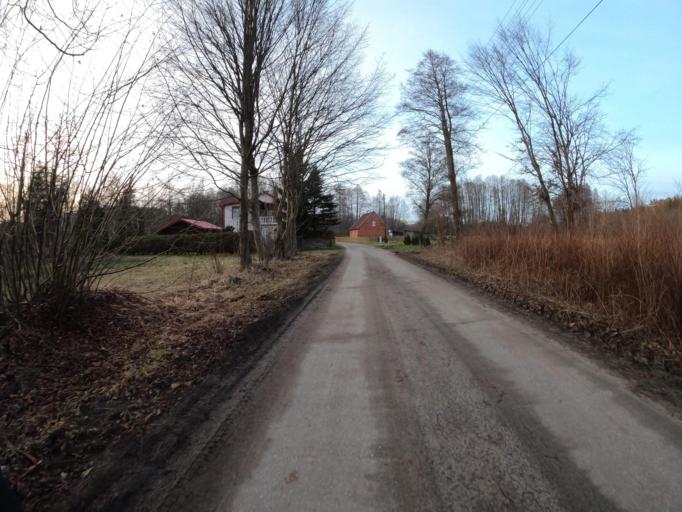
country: PL
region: West Pomeranian Voivodeship
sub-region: Powiat koszalinski
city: Polanow
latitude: 54.2017
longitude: 16.7139
